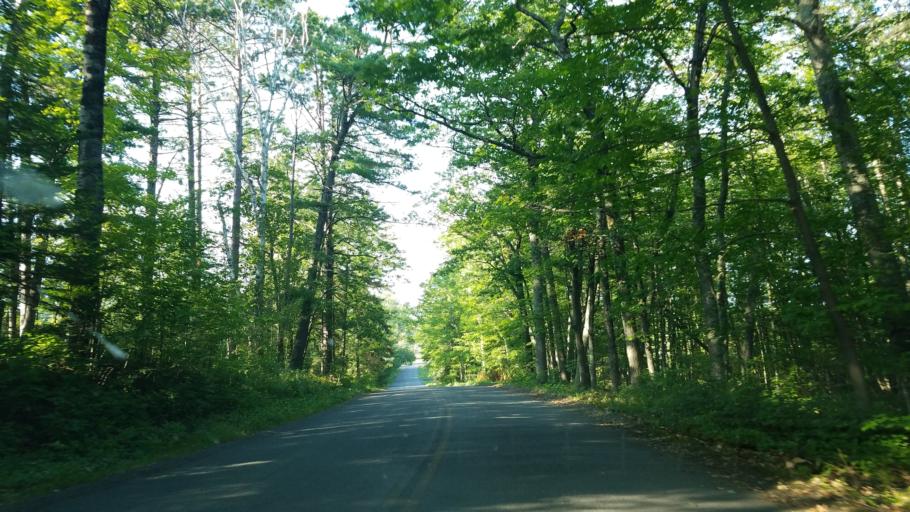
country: US
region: Wisconsin
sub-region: Bayfield County
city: Washburn
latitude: 46.7669
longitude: -90.7805
